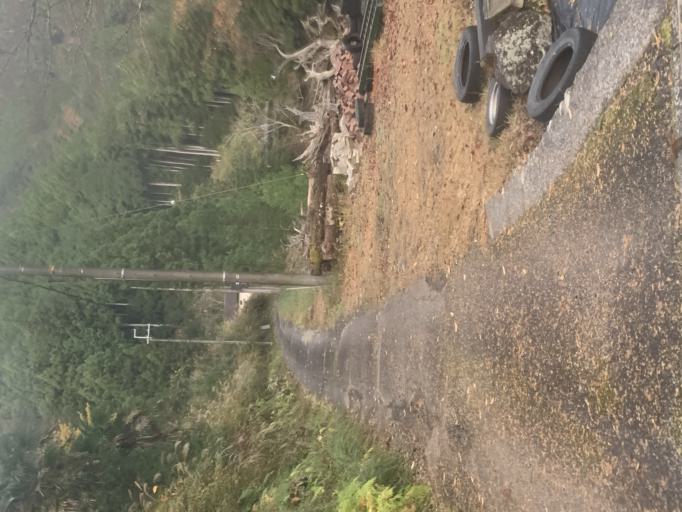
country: JP
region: Mie
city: Owase
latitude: 34.0427
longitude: 135.9568
